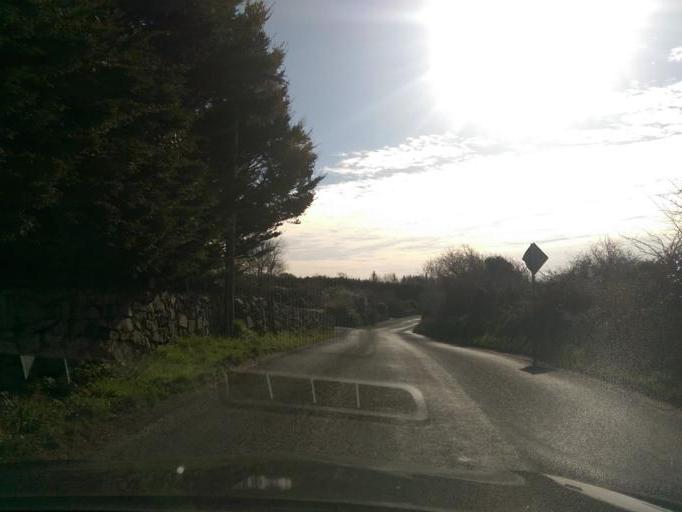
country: IE
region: Connaught
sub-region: County Galway
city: Oranmore
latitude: 53.2363
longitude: -8.9467
